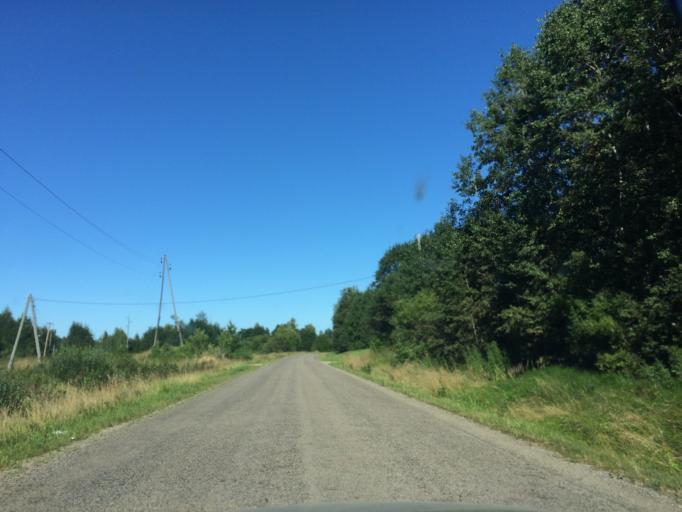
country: LV
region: Rezekne
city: Rezekne
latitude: 56.4921
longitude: 27.2724
